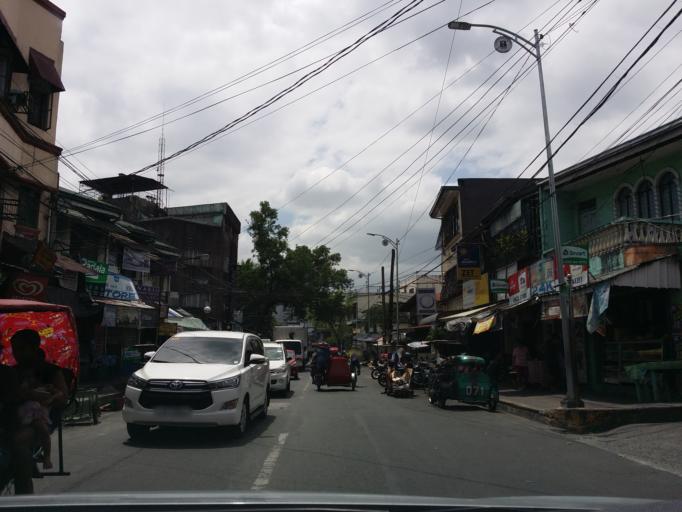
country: PH
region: Metro Manila
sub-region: Mandaluyong
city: Mandaluyong City
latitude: 14.5789
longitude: 121.0129
